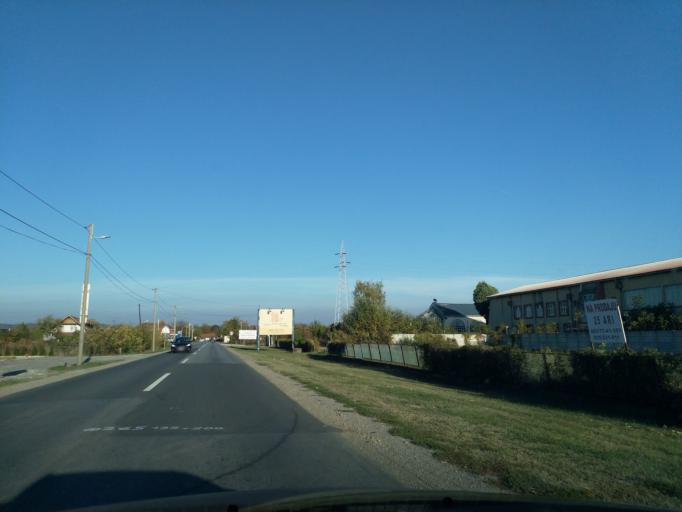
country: RS
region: Central Serbia
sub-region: Pomoravski Okrug
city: Svilajnac
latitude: 44.2294
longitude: 21.1770
